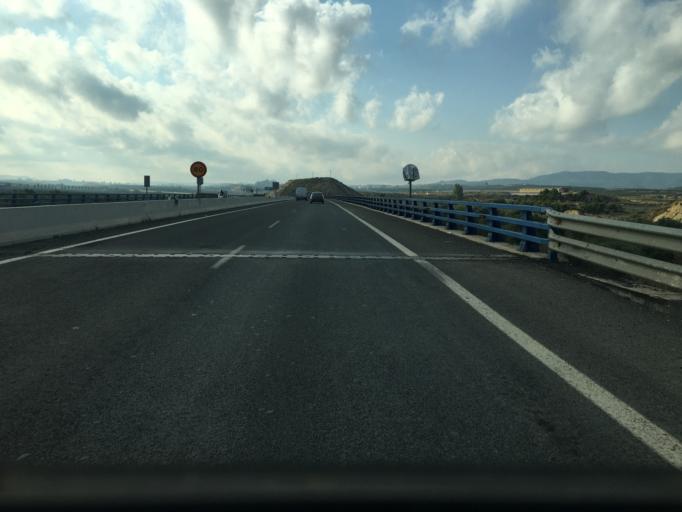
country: ES
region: Murcia
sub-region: Murcia
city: Beniel
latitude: 37.9990
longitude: -1.0087
